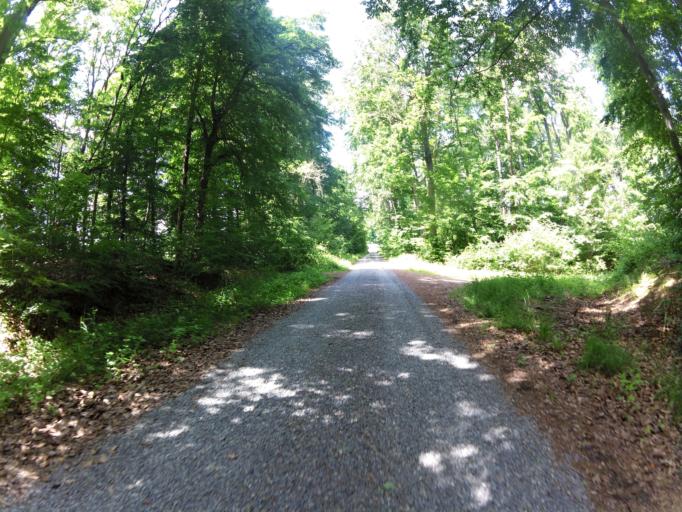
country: DE
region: Bavaria
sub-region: Regierungsbezirk Unterfranken
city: Uettingen
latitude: 49.7686
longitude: 9.7613
